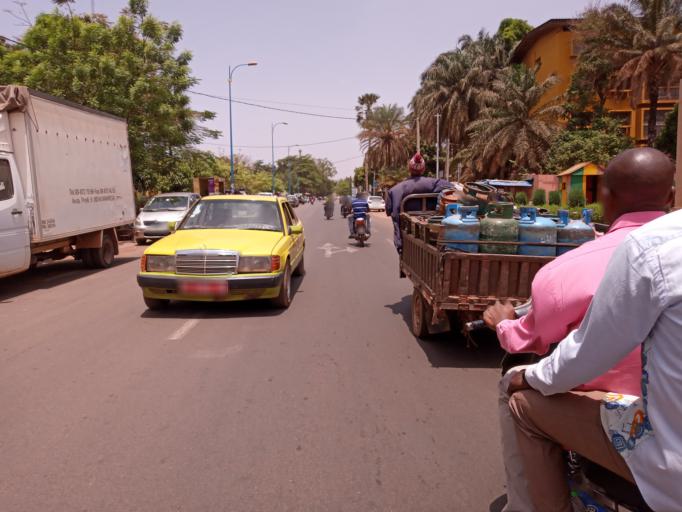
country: ML
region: Bamako
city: Bamako
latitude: 12.6328
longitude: -7.9993
